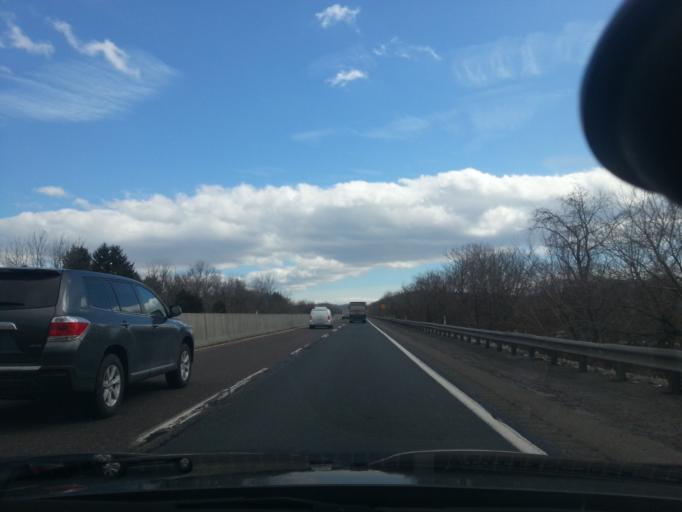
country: US
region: Pennsylvania
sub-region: Lehigh County
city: Emmaus
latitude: 40.5284
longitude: -75.5179
